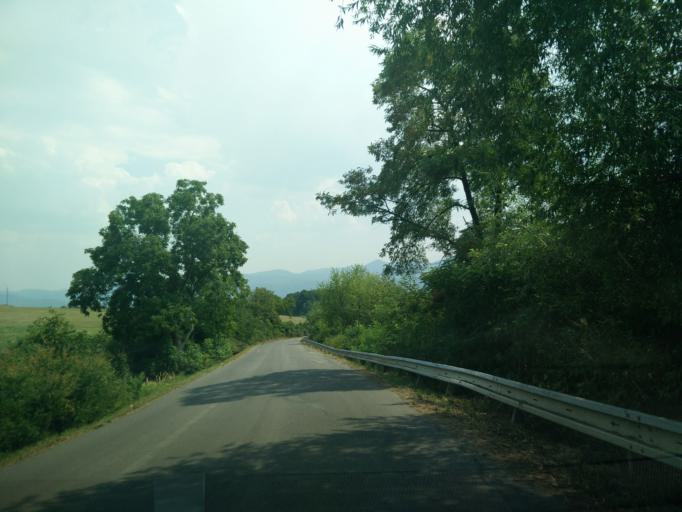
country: SK
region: Banskobystricky
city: Zarnovica
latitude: 48.5762
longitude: 18.7445
